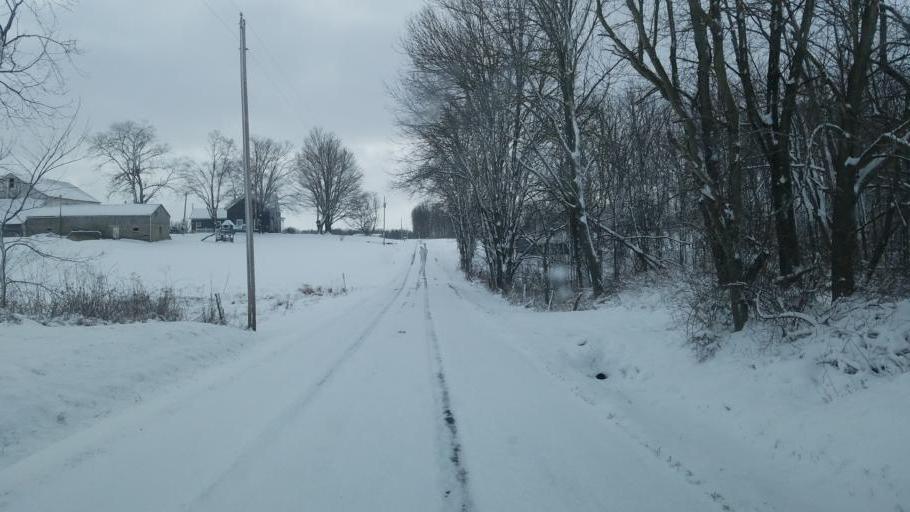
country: US
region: Ohio
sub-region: Knox County
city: Fredericktown
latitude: 40.5540
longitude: -82.5855
